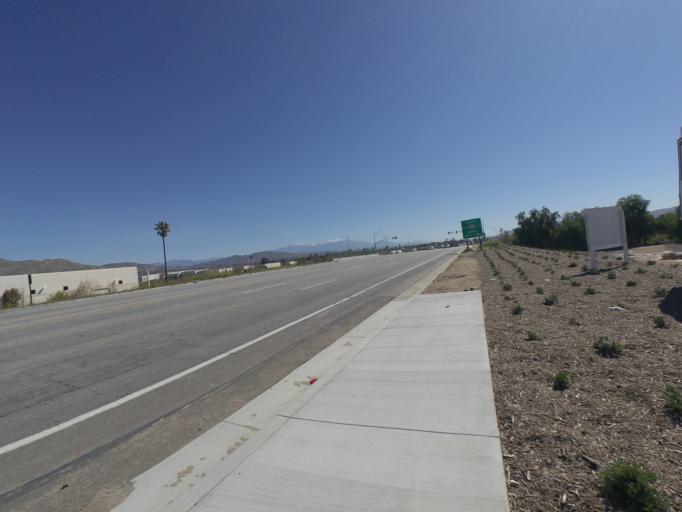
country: US
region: California
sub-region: Riverside County
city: March Air Force Base
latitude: 33.9166
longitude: -117.2910
